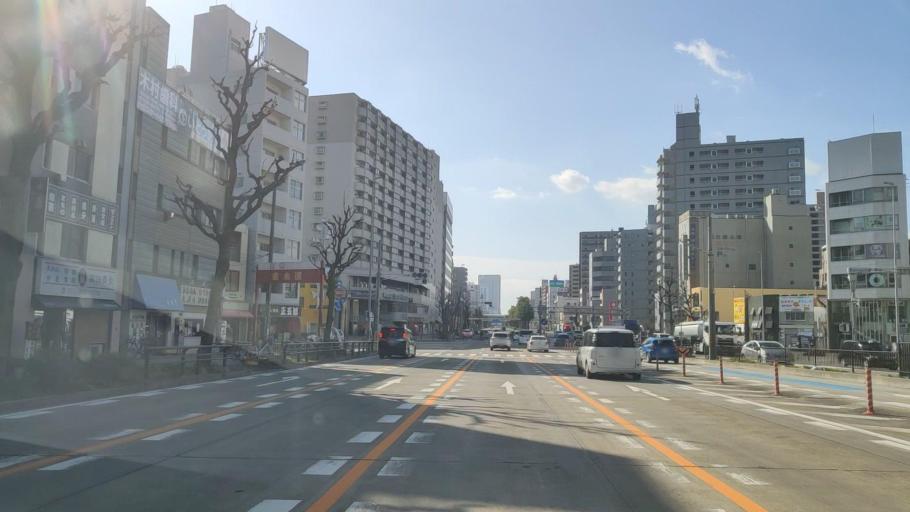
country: JP
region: Aichi
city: Nagoya-shi
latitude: 35.1588
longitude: 136.8985
